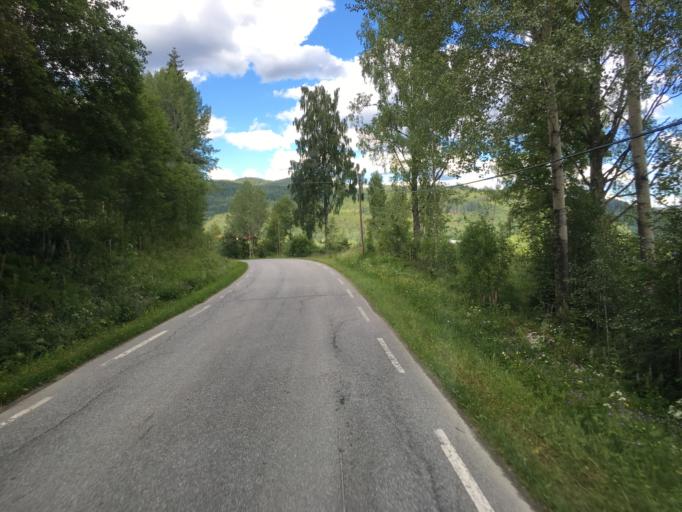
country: NO
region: Oppland
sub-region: Sondre Land
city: Hov
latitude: 60.5909
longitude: 10.2973
